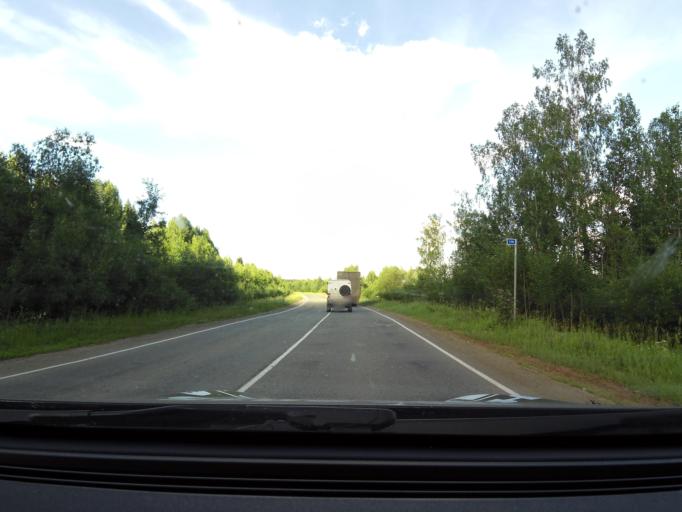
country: RU
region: Kirov
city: Belorechensk
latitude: 58.7074
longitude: 52.2674
